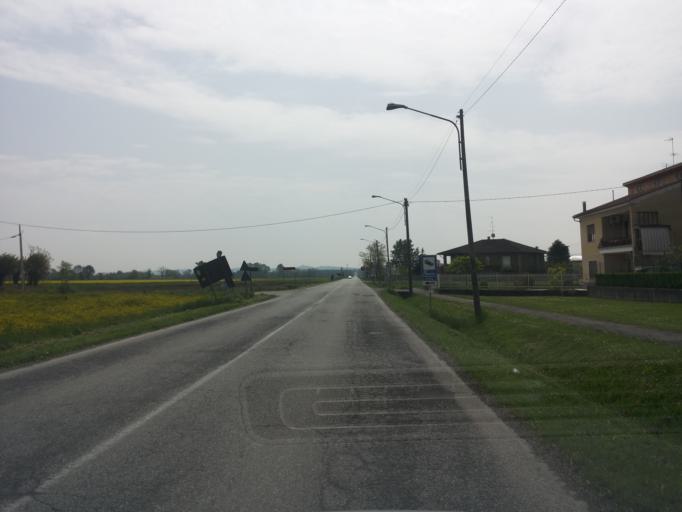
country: IT
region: Piedmont
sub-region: Provincia di Alessandria
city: Occimiano
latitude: 45.0581
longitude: 8.5105
